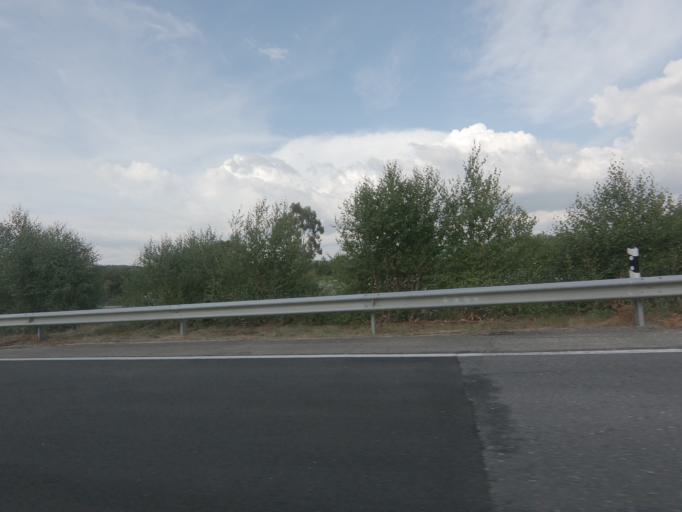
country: ES
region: Galicia
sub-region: Provincia de Ourense
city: Ambia
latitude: 42.1595
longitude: -7.7600
